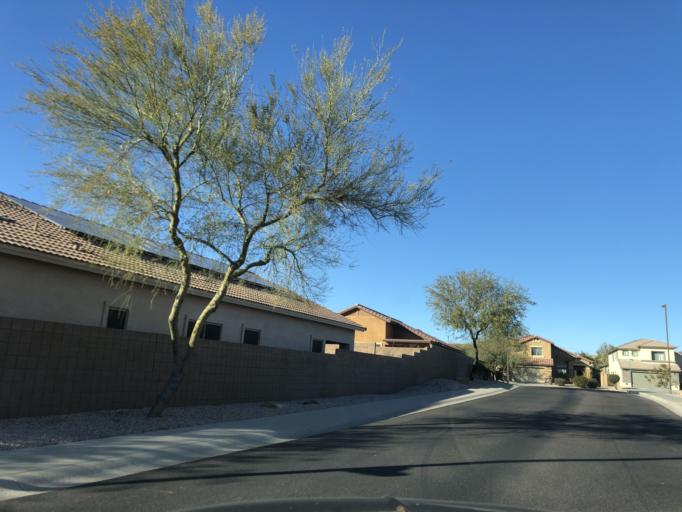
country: US
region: Arizona
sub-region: Maricopa County
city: Buckeye
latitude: 33.4249
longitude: -112.6070
